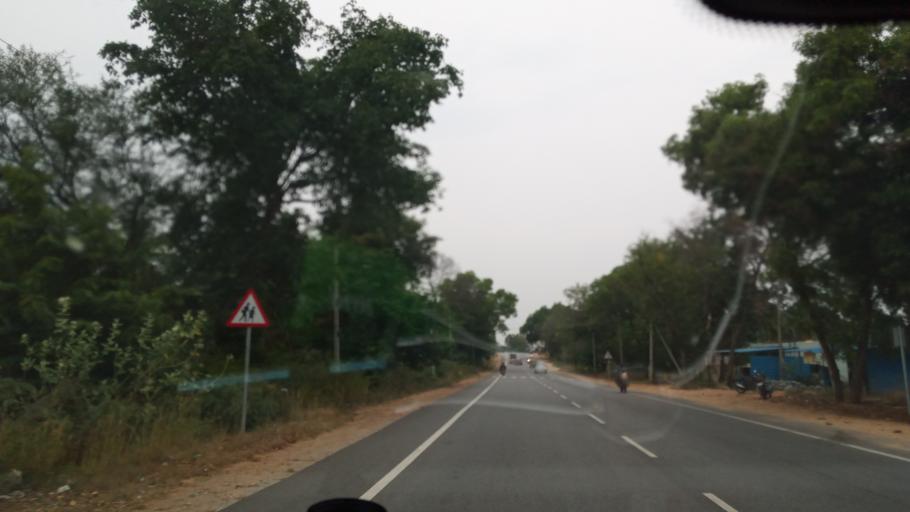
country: IN
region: Karnataka
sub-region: Mandya
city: Belluru
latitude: 12.9427
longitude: 76.7515
